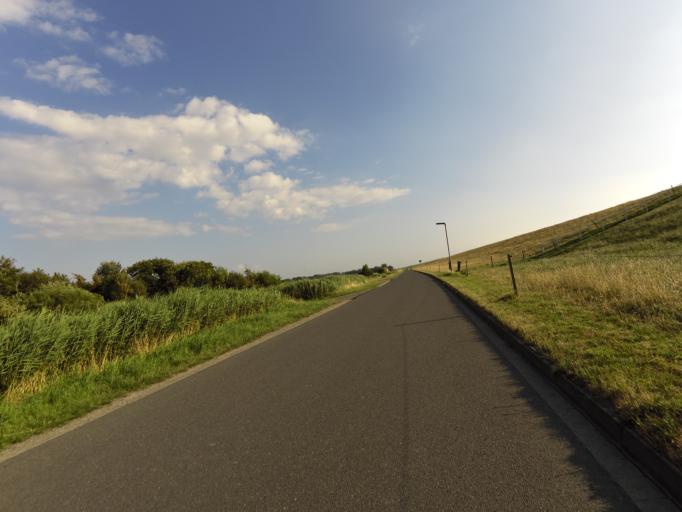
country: DE
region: Lower Saxony
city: Nordholz
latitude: 53.7843
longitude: 8.5512
